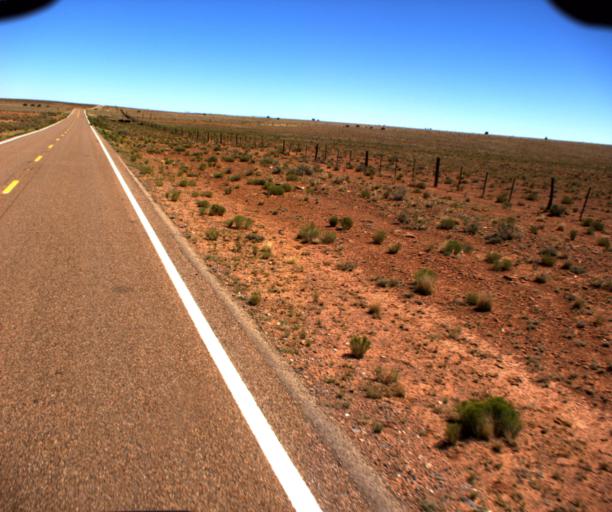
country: US
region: Arizona
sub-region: Navajo County
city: Winslow
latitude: 34.8524
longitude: -110.6654
